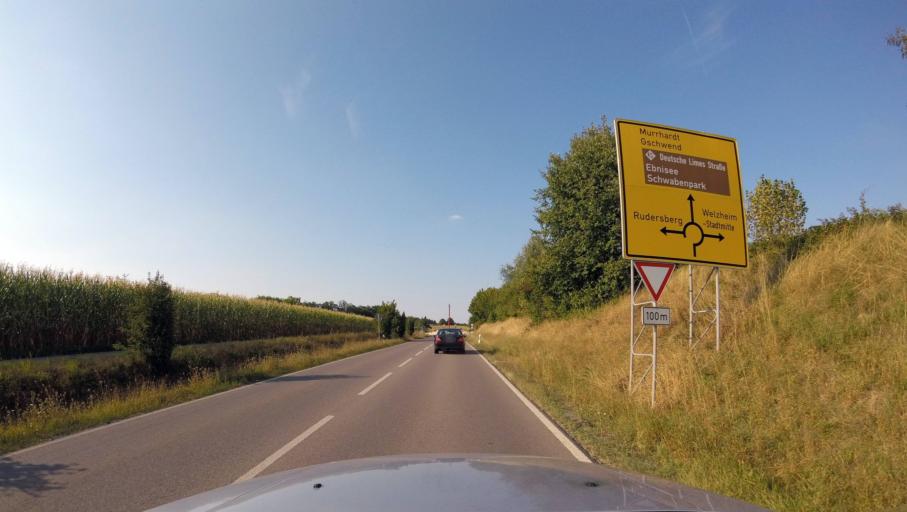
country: DE
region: Baden-Wuerttemberg
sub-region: Regierungsbezirk Stuttgart
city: Welzheim
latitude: 48.8762
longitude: 9.6214
